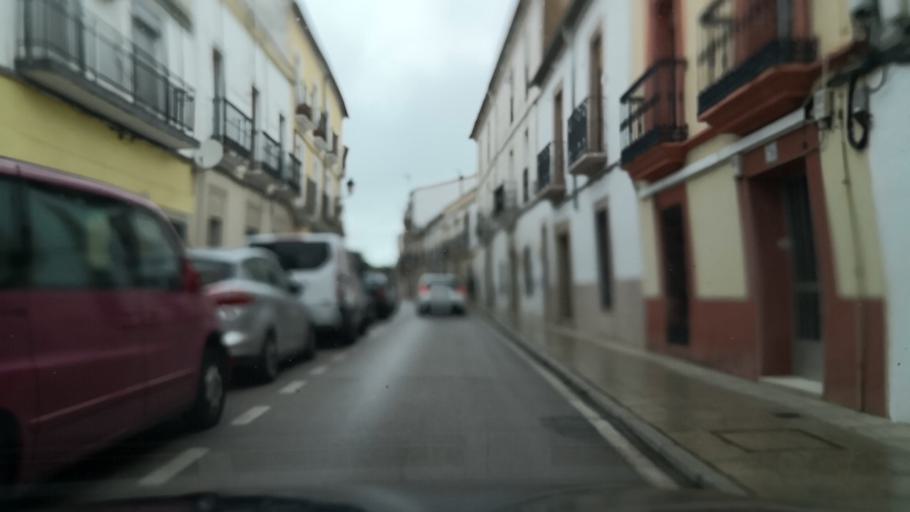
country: ES
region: Extremadura
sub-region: Provincia de Caceres
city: Caceres
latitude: 39.4781
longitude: -6.3736
